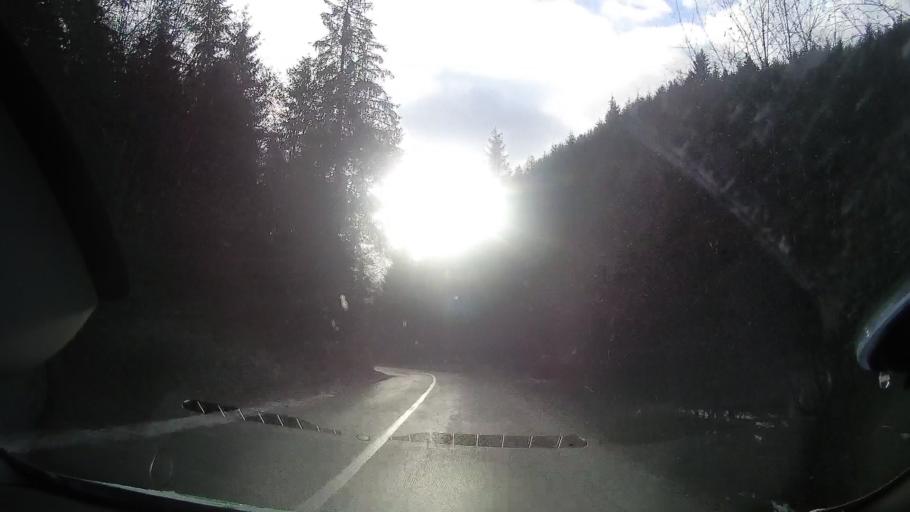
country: RO
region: Alba
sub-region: Comuna Albac
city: Albac
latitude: 46.4738
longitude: 22.9634
